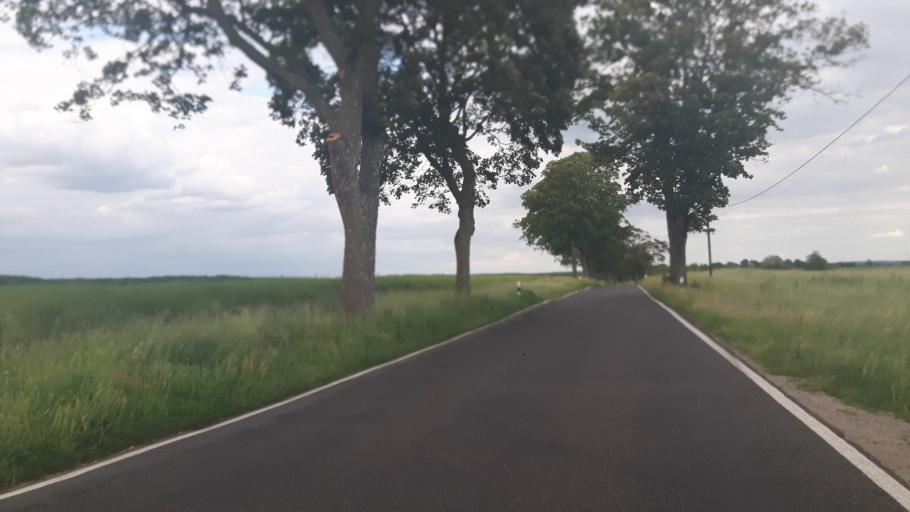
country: DE
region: Brandenburg
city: Hohenfinow
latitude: 52.7718
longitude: 13.8681
